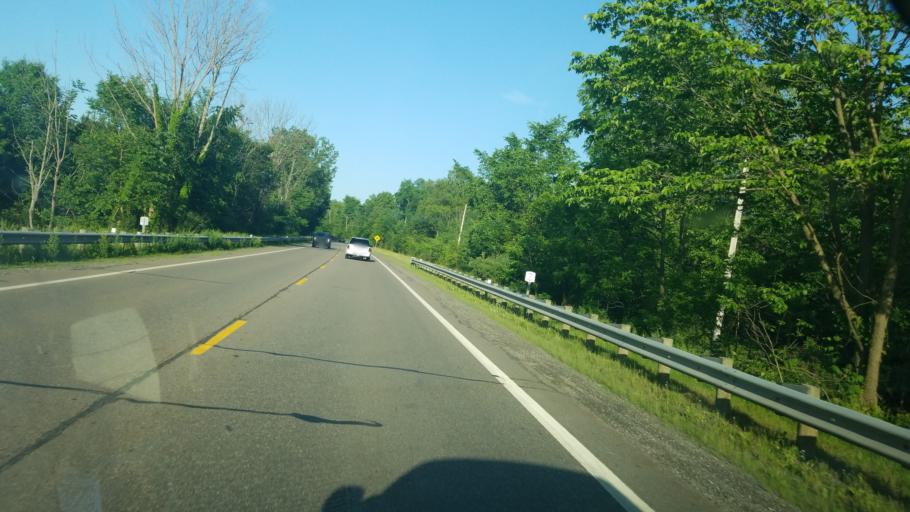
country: US
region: Ohio
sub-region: Portage County
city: Ravenna
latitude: 41.1516
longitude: -81.1805
